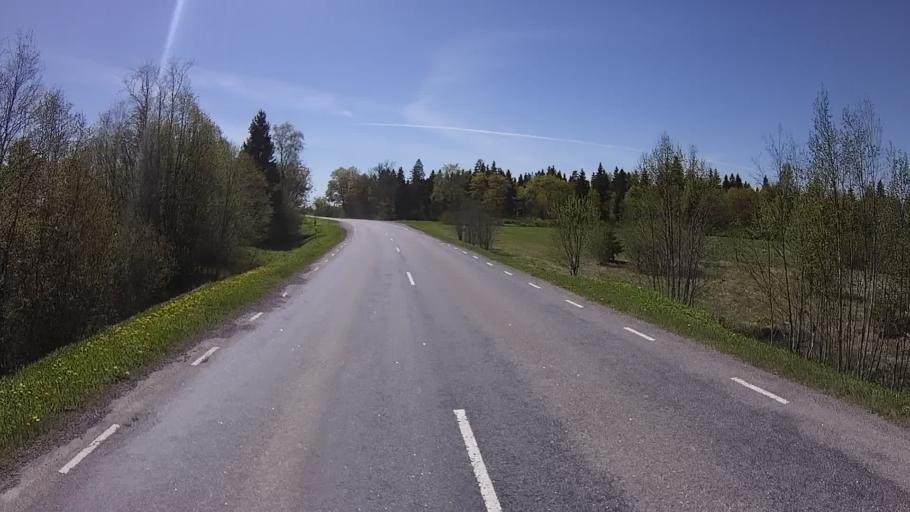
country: EE
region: Harju
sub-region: Raasiku vald
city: Raasiku
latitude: 59.0800
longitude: 25.1675
